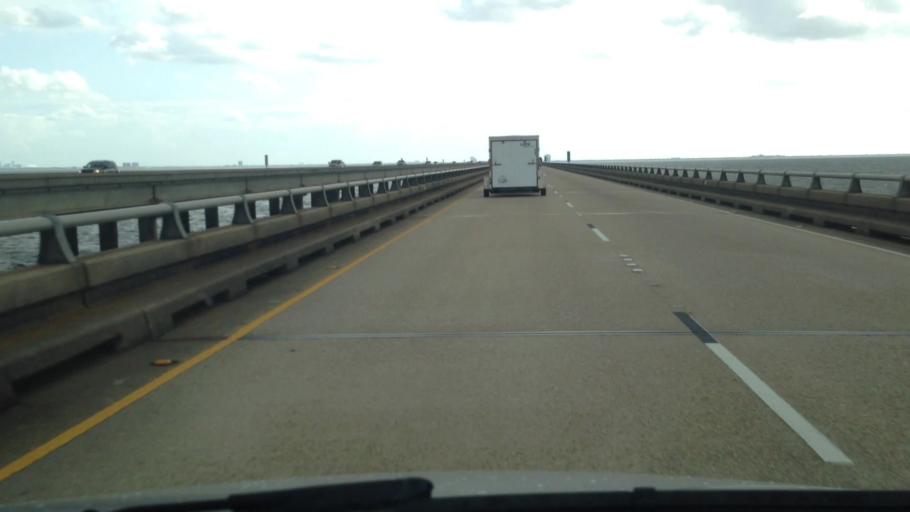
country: US
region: Louisiana
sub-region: Jefferson Parish
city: Metairie
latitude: 30.1034
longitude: -90.1398
